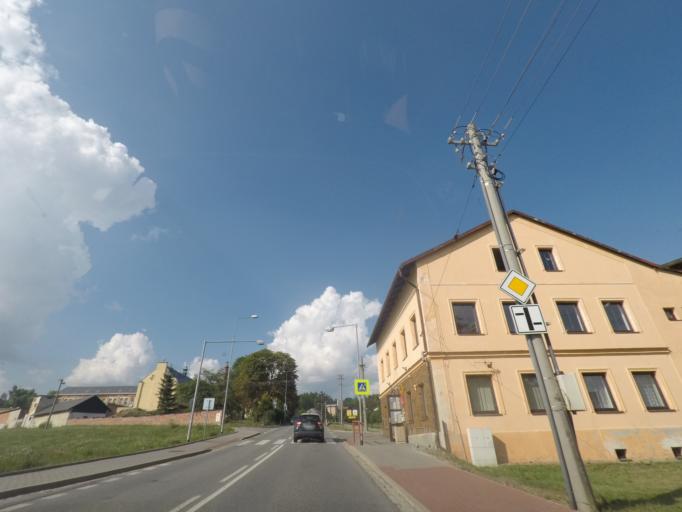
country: CZ
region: Kralovehradecky
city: Dvur Kralove nad Labem
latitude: 50.4603
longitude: 15.8611
